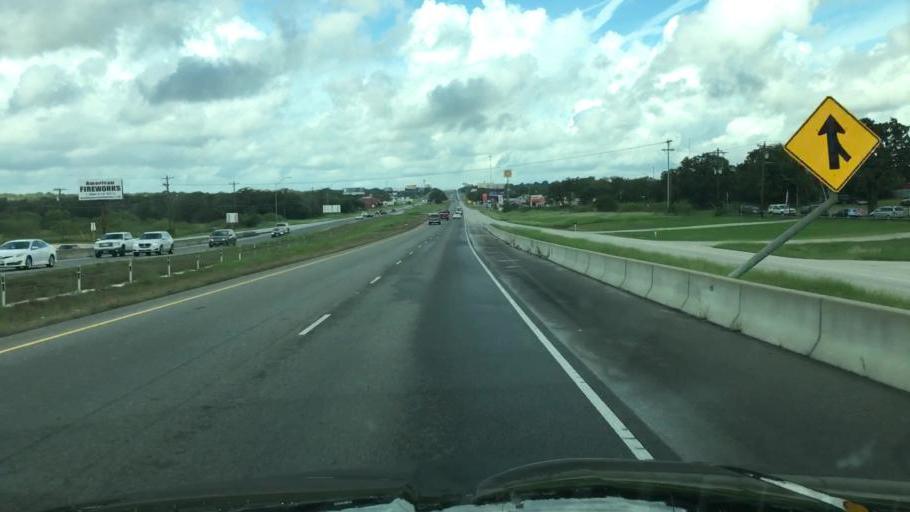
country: US
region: Texas
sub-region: Bastrop County
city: Wyldwood
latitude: 30.1140
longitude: -97.4181
